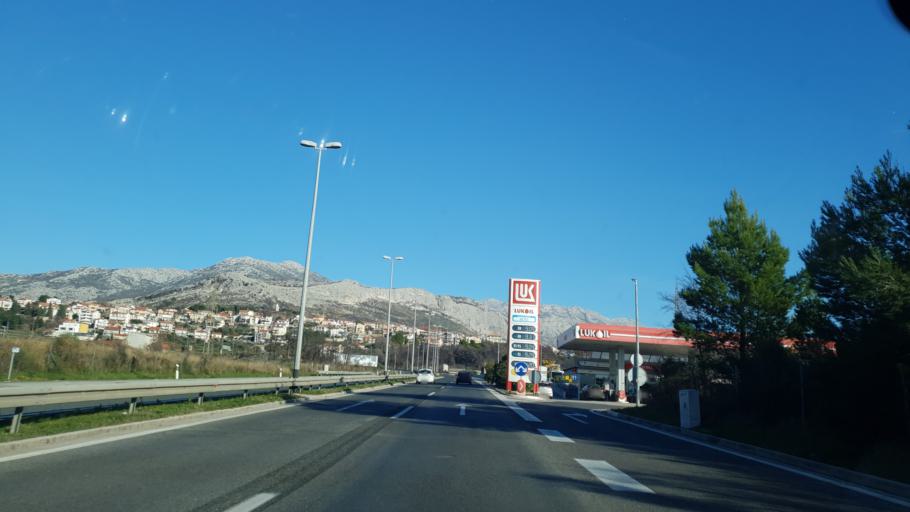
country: HR
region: Splitsko-Dalmatinska
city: Kamen
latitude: 43.5284
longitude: 16.5053
